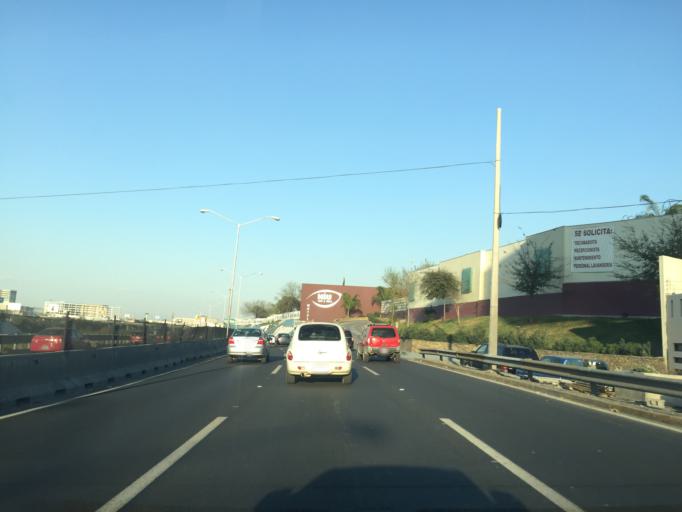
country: MX
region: Nuevo Leon
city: Guadalupe
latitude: 25.6842
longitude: -100.2509
